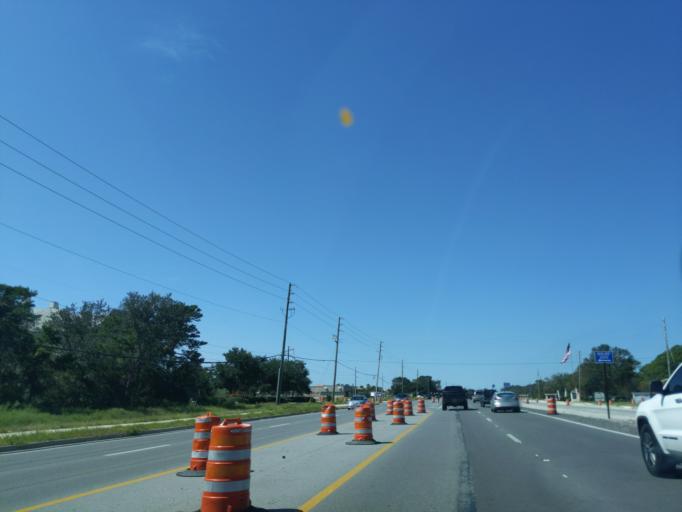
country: US
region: Florida
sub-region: Walton County
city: Miramar Beach
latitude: 30.3849
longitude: -86.3916
